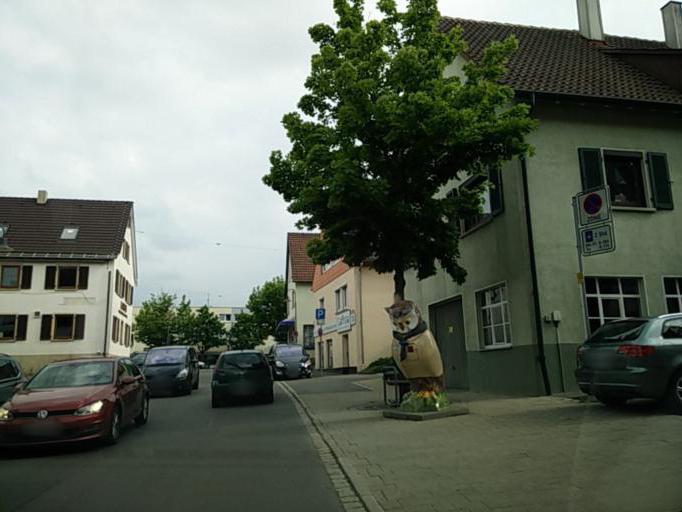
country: DE
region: Baden-Wuerttemberg
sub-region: Regierungsbezirk Stuttgart
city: Holzgerlingen
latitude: 48.6386
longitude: 9.0118
